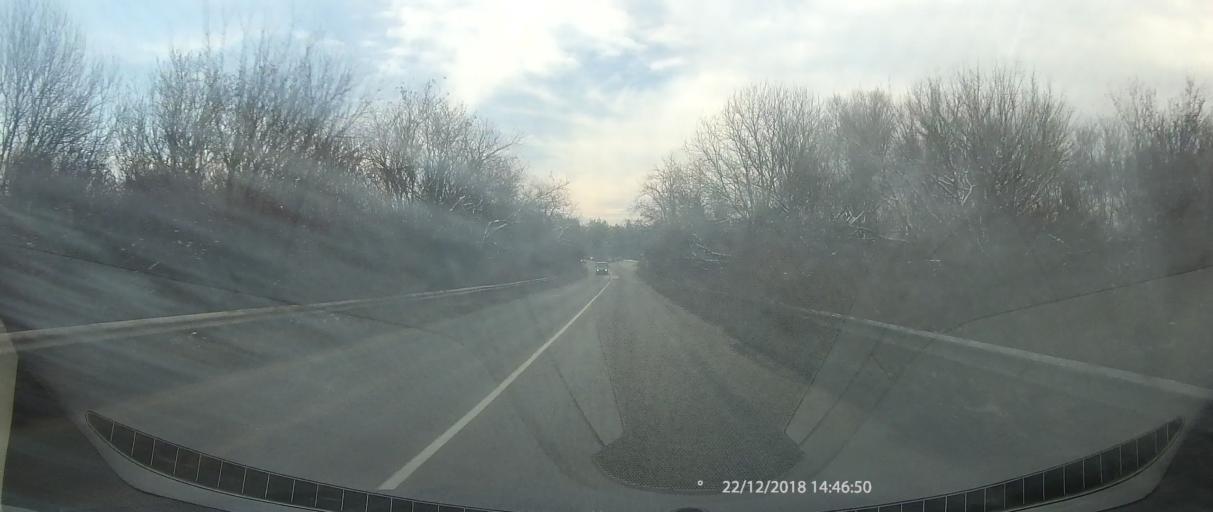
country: BG
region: Veliko Turnovo
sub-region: Obshtina Pavlikeni
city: Pavlikeni
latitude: 43.4148
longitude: 25.3705
